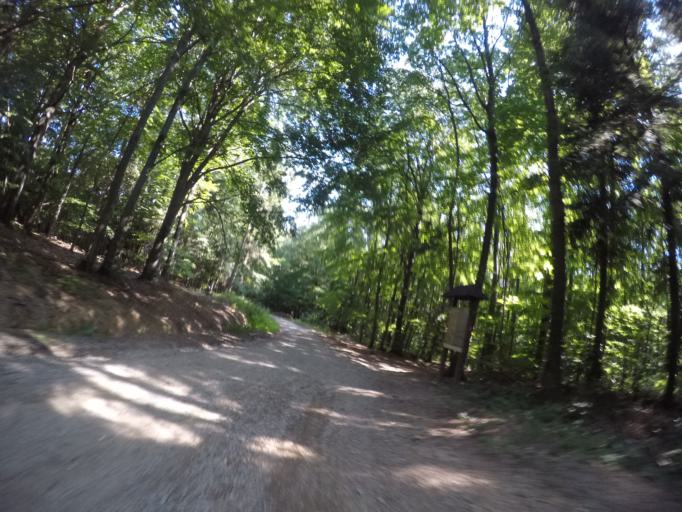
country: SK
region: Kosicky
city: Kosice
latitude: 48.7411
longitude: 21.1934
